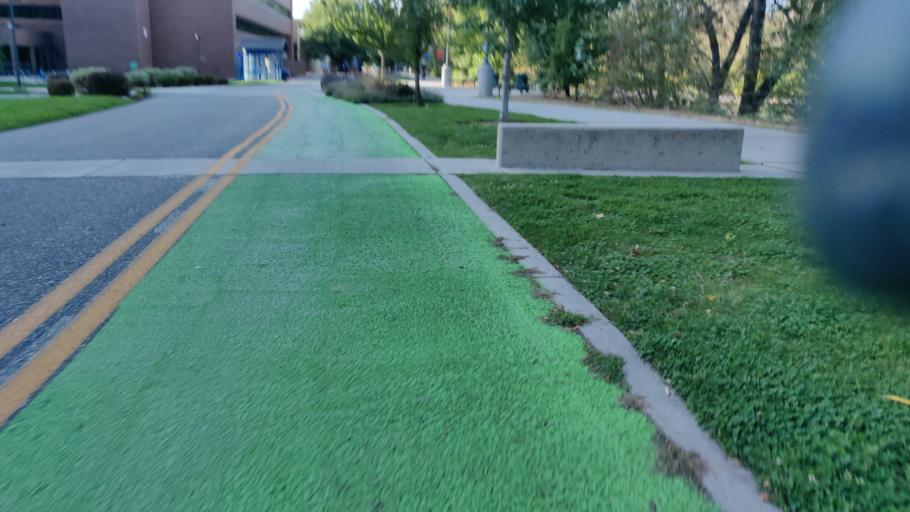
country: US
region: Idaho
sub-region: Ada County
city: Boise
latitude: 43.6057
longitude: -116.2049
